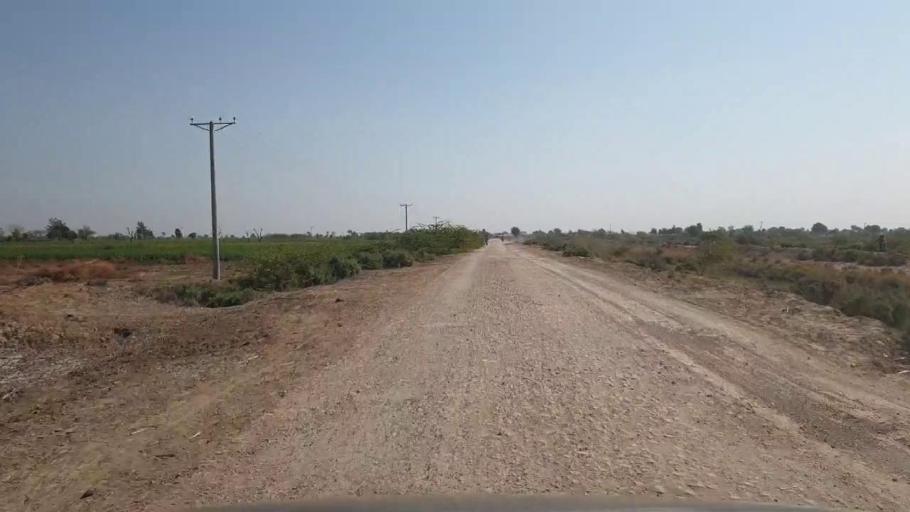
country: PK
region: Sindh
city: Samaro
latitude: 25.2528
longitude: 69.2734
